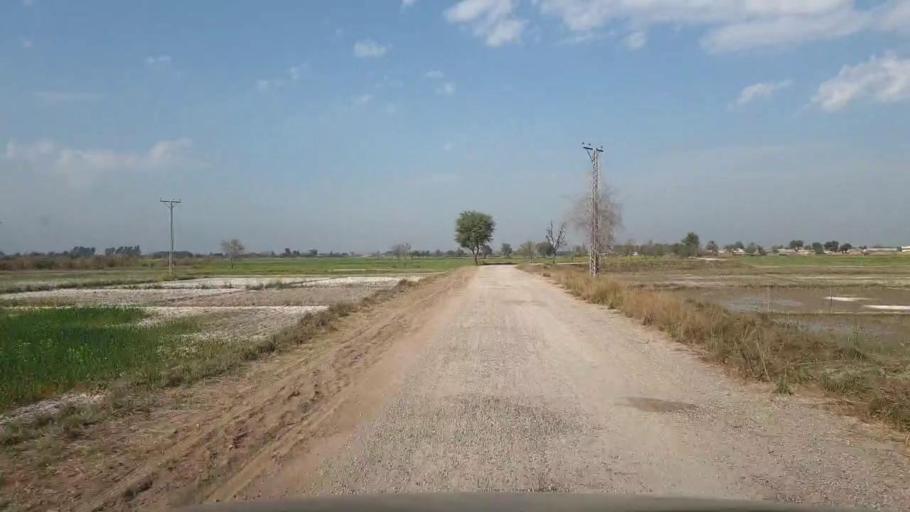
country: PK
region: Sindh
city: Sakrand
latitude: 26.0167
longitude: 68.4168
